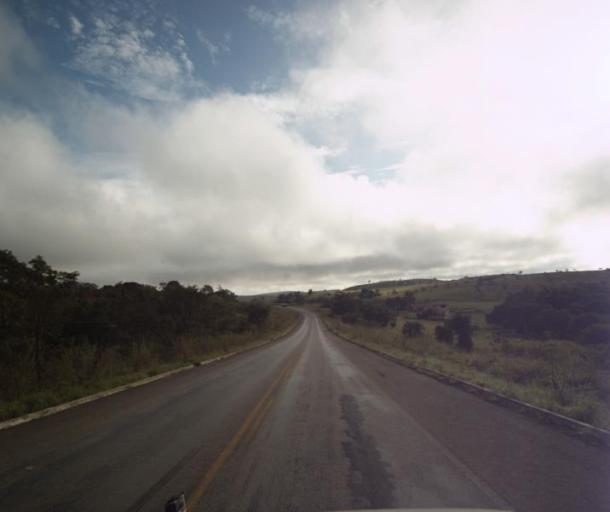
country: BR
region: Goias
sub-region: Pirenopolis
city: Pirenopolis
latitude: -15.7505
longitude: -48.7264
